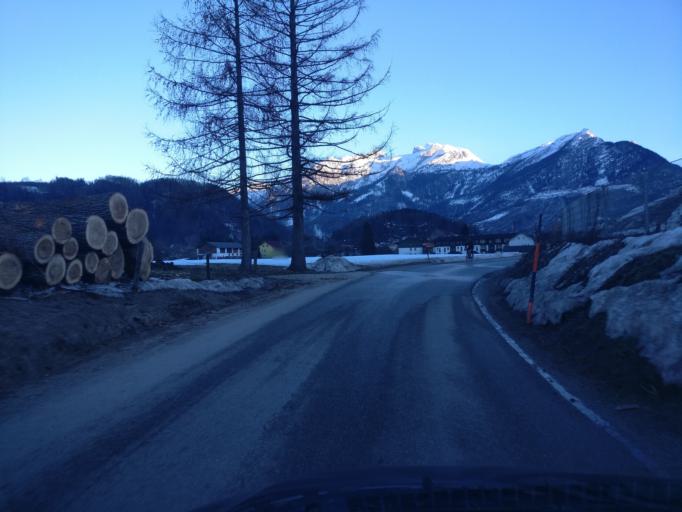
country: AT
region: Salzburg
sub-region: Politischer Bezirk Hallein
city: Golling an der Salzach
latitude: 47.6049
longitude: 13.1627
